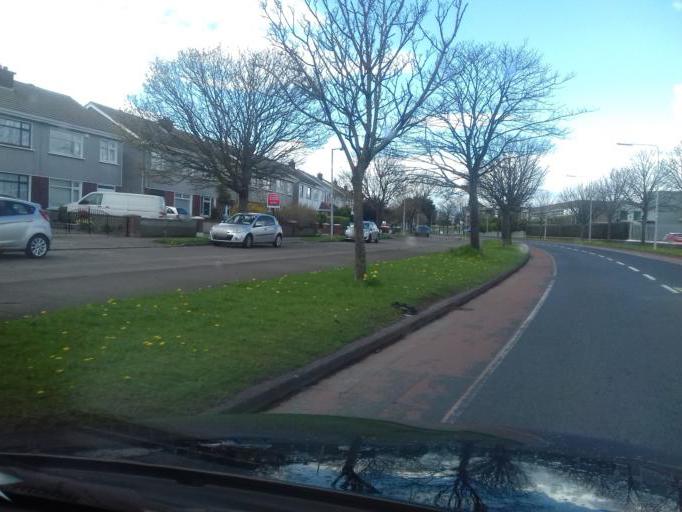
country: IE
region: Leinster
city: Donaghmede
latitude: 53.3894
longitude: -6.1532
